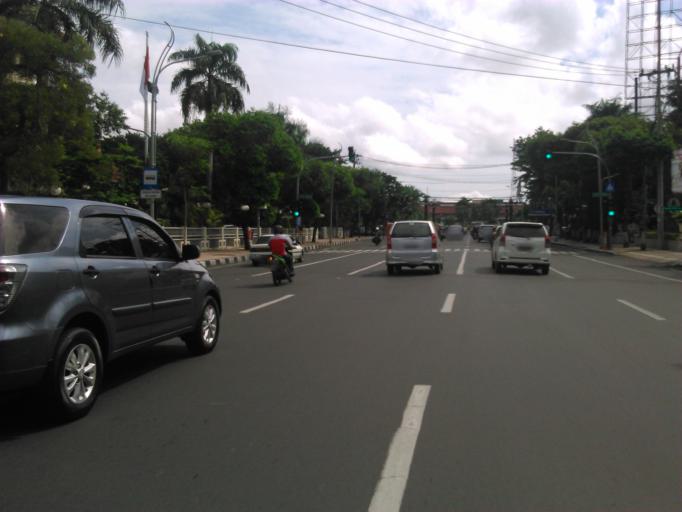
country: ID
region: East Java
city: Pacarkeling
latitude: -7.2635
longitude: 112.7459
